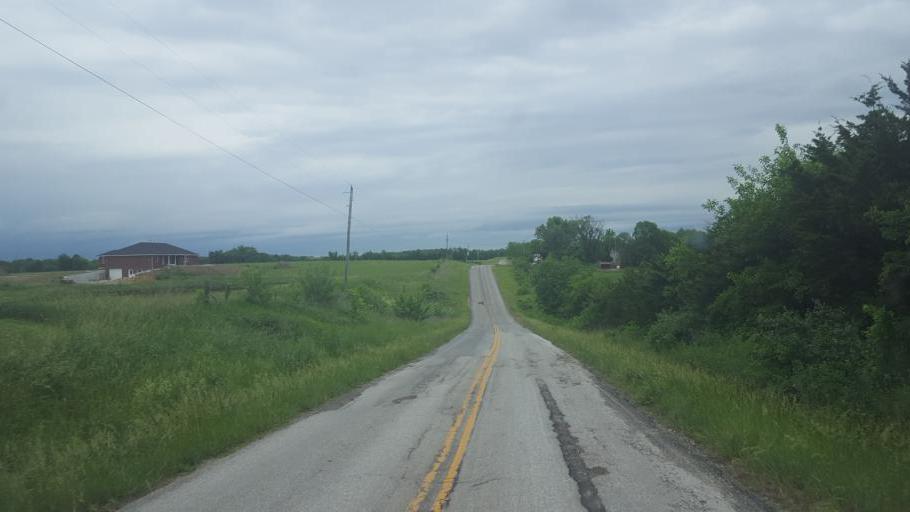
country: US
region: Missouri
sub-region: Moniteau County
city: California
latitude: 38.7640
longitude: -92.6054
